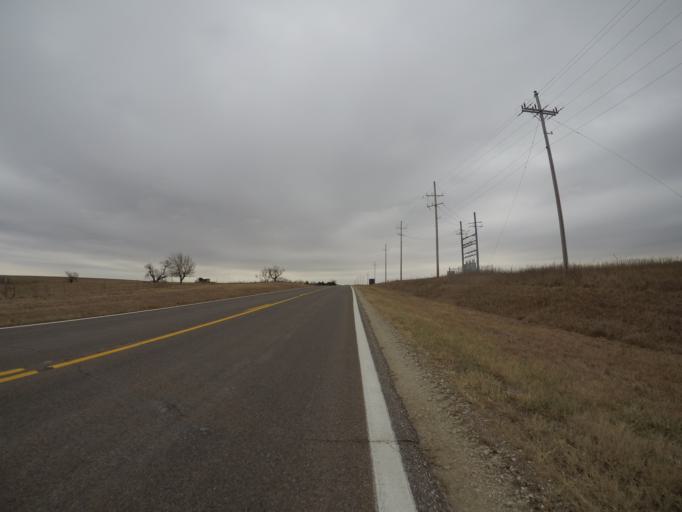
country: US
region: Kansas
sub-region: Wabaunsee County
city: Alma
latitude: 38.8670
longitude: -96.1275
